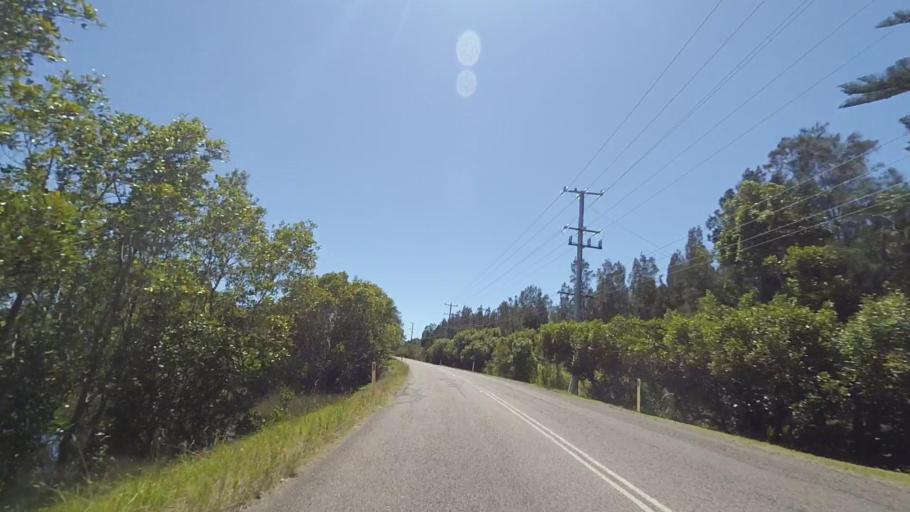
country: AU
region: New South Wales
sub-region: Port Stephens Shire
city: Medowie
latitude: -32.7779
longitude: 151.9664
